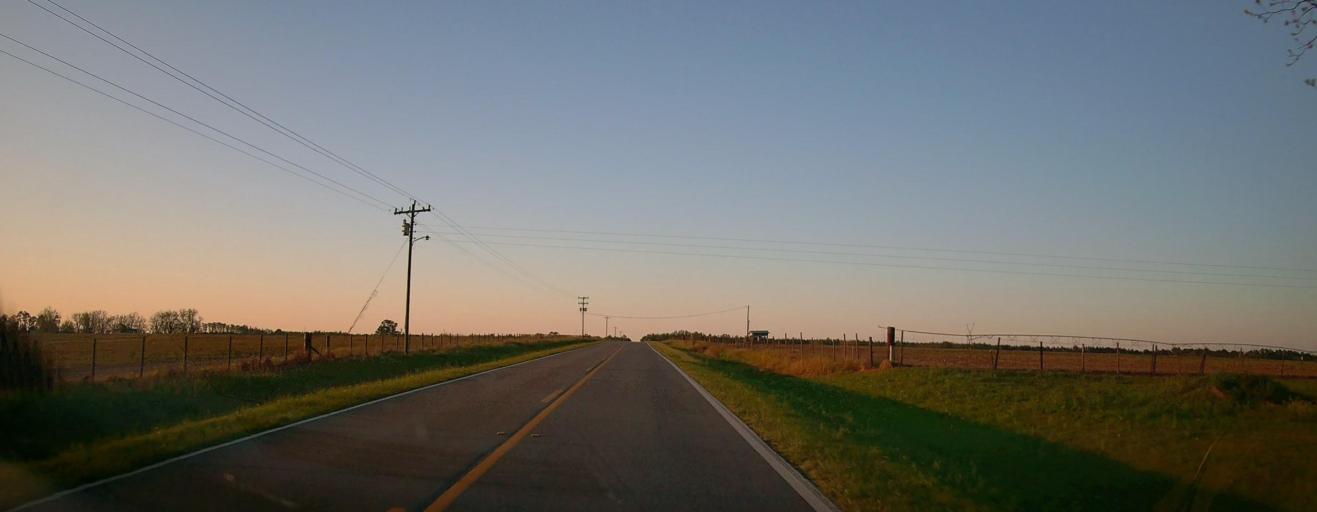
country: US
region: Georgia
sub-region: Ben Hill County
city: Fitzgerald
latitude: 31.7259
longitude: -83.3099
